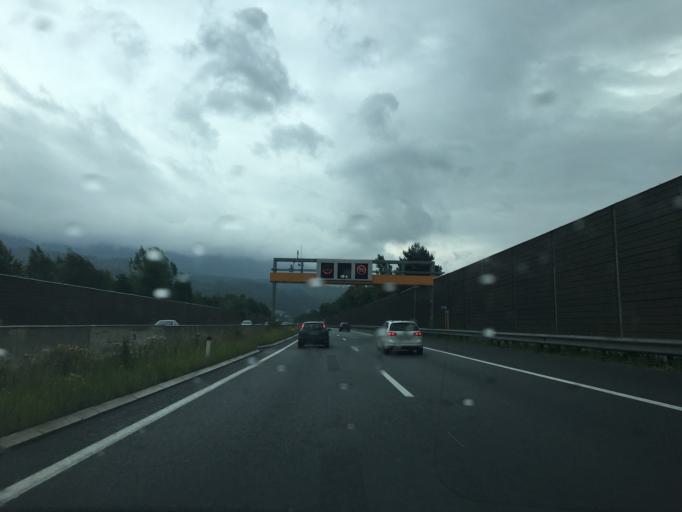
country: AT
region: Tyrol
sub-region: Politischer Bezirk Innsbruck Land
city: Volders
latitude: 47.2866
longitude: 11.5580
